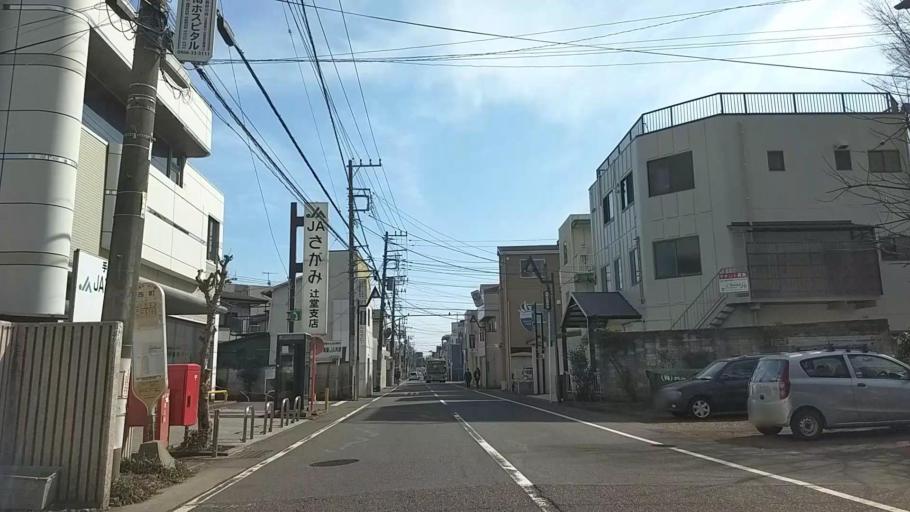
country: JP
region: Kanagawa
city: Fujisawa
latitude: 35.3318
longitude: 139.4510
